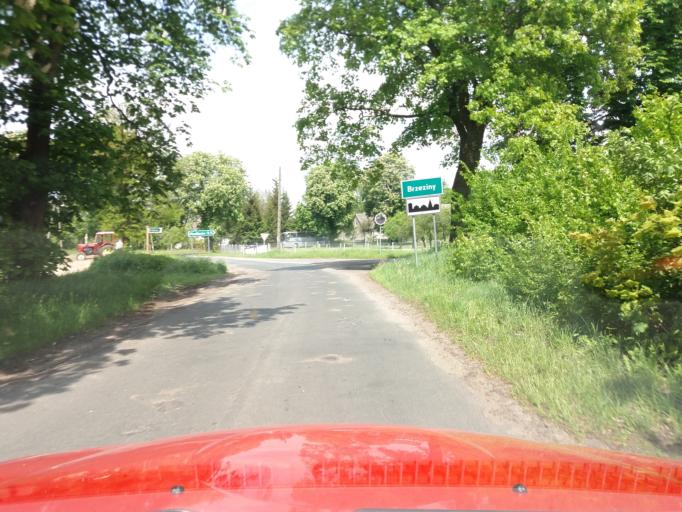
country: PL
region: West Pomeranian Voivodeship
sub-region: Powiat choszczenski
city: Bierzwnik
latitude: 53.1444
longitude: 15.6767
